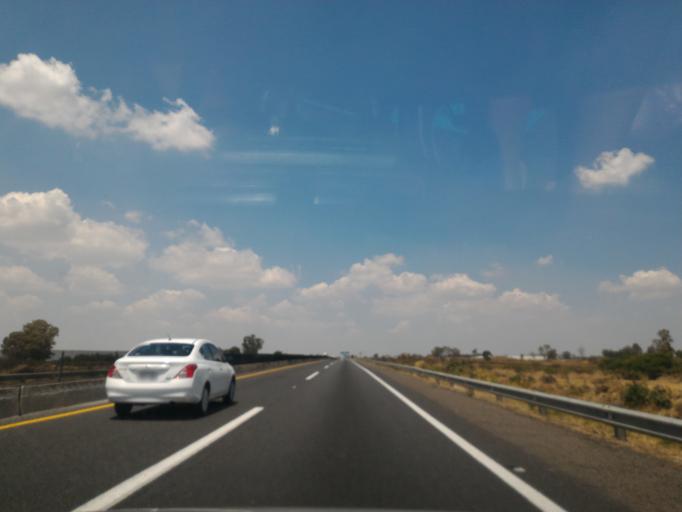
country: MX
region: Jalisco
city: Tepatitlan de Morelos
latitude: 20.8826
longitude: -102.7297
